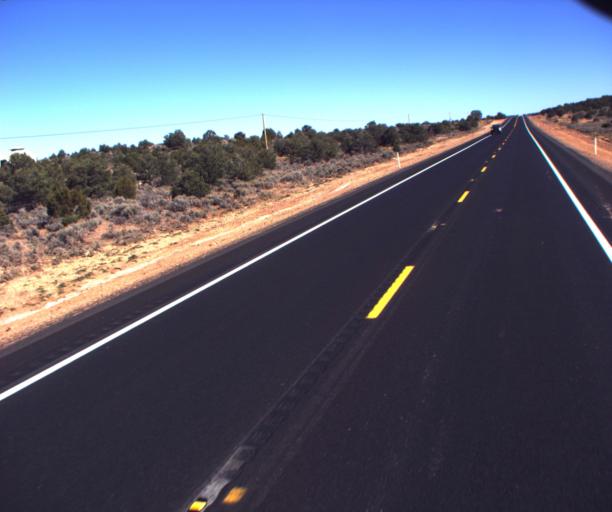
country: US
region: Arizona
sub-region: Apache County
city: Ganado
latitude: 35.7165
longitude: -109.4207
